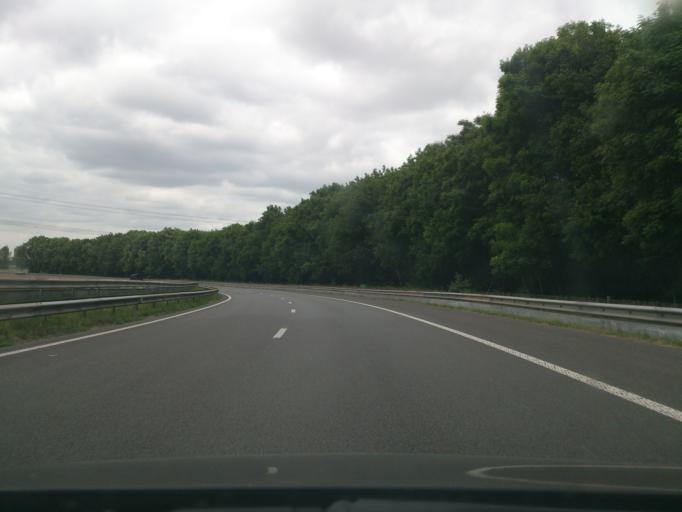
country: NL
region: Gelderland
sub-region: Gemeente Wijchen
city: Bergharen
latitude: 51.8147
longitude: 5.6783
